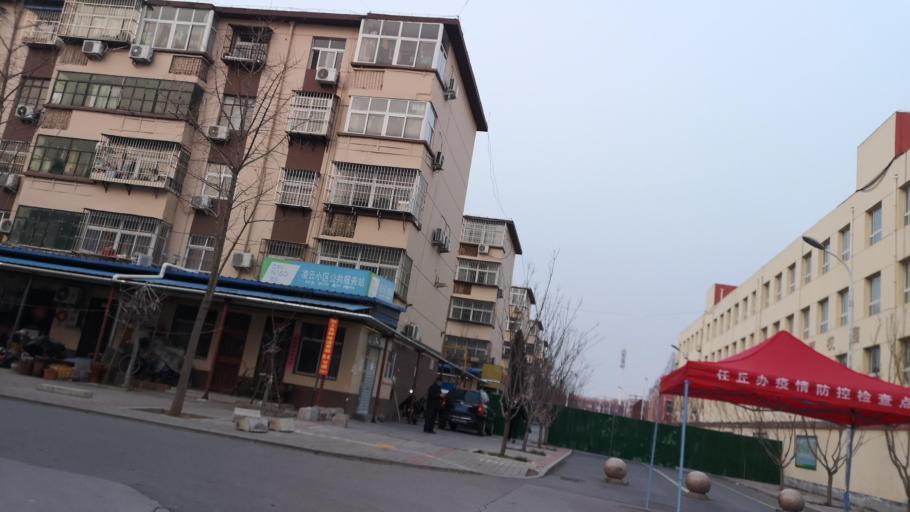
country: CN
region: Henan Sheng
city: Zhongyuanlu
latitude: 35.7824
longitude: 115.0750
